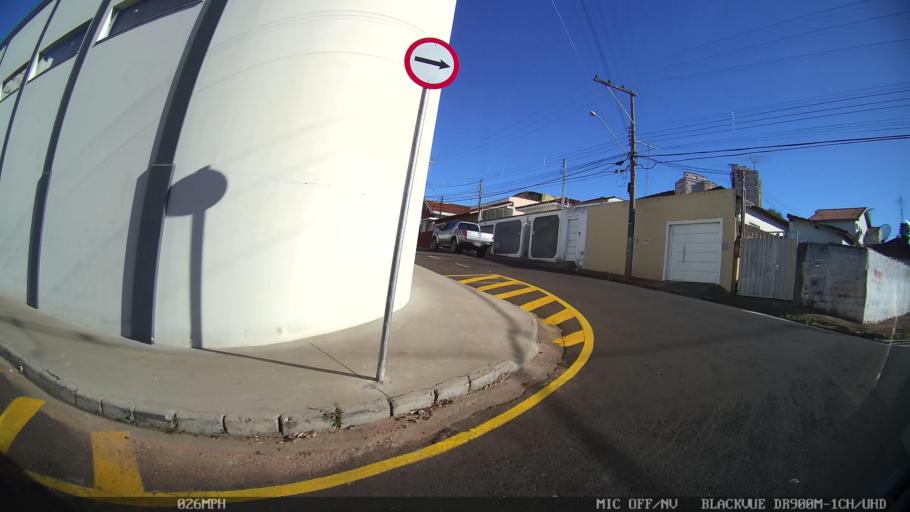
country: BR
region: Sao Paulo
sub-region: Franca
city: Franca
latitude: -20.5488
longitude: -47.4041
